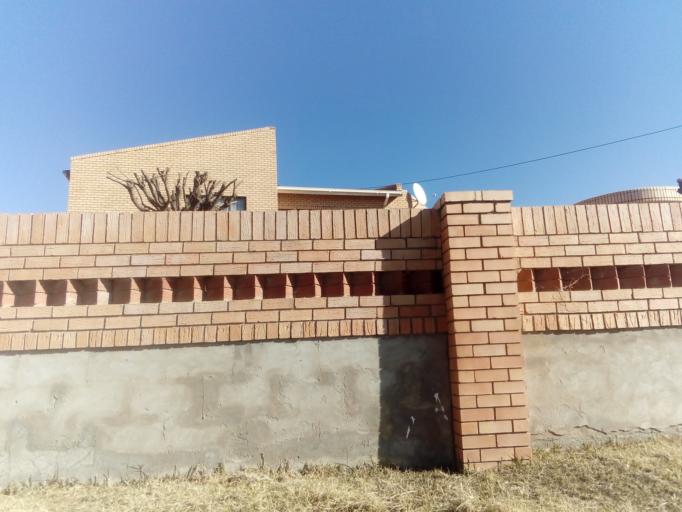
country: LS
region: Berea
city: Teyateyaneng
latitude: -29.1430
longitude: 27.7647
